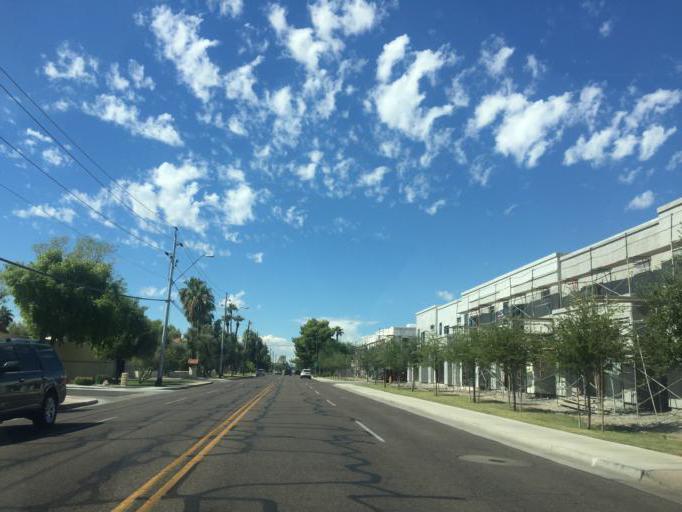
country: US
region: Arizona
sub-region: Maricopa County
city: Phoenix
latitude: 33.5166
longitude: -112.0772
